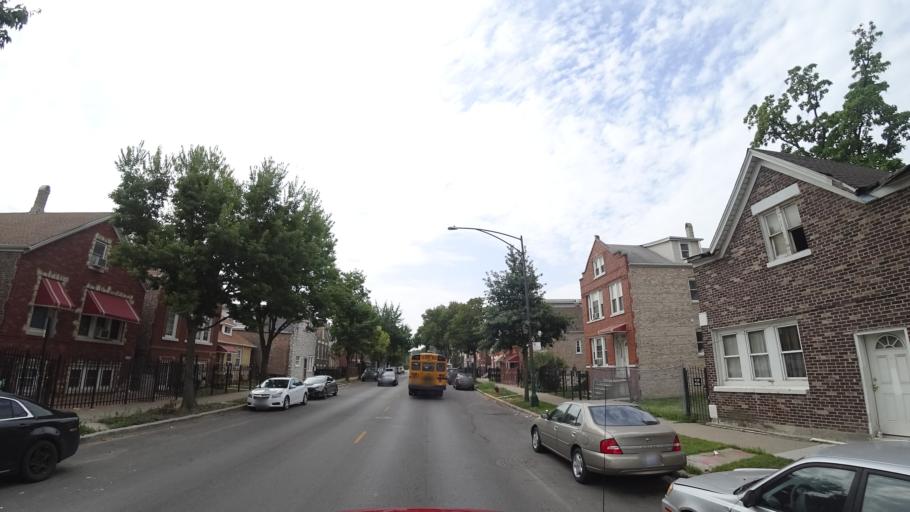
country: US
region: Illinois
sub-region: Cook County
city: Cicero
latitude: 41.8383
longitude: -87.7146
